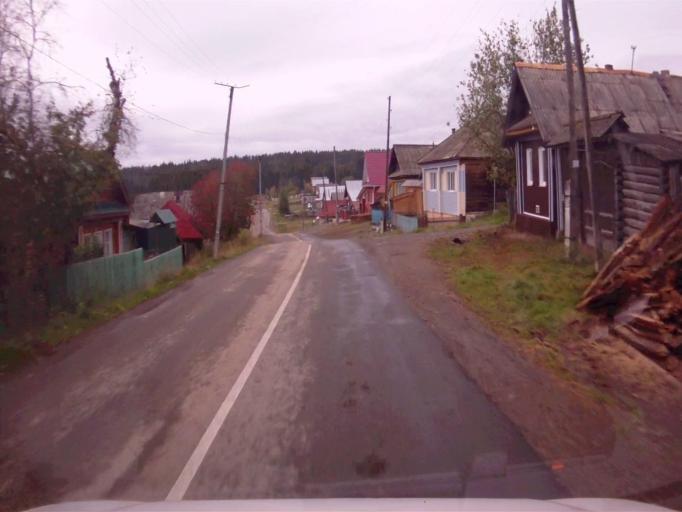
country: RU
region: Chelyabinsk
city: Nyazepetrovsk
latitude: 56.0628
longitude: 59.5737
